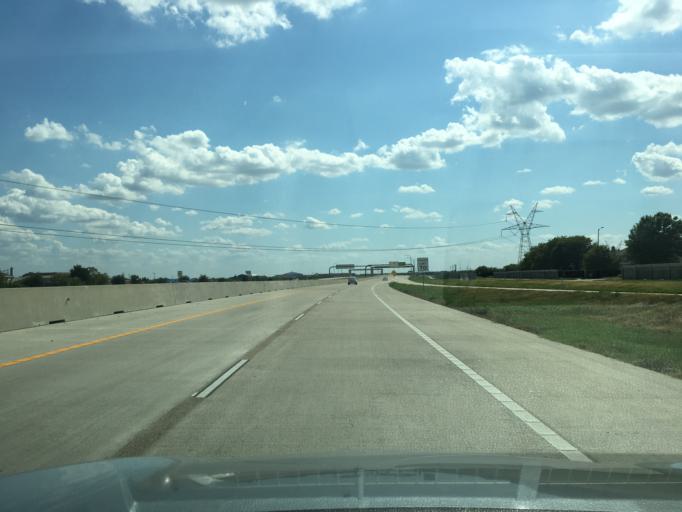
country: US
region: Texas
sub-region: Tarrant County
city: Mansfield
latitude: 32.6317
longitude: -97.0661
